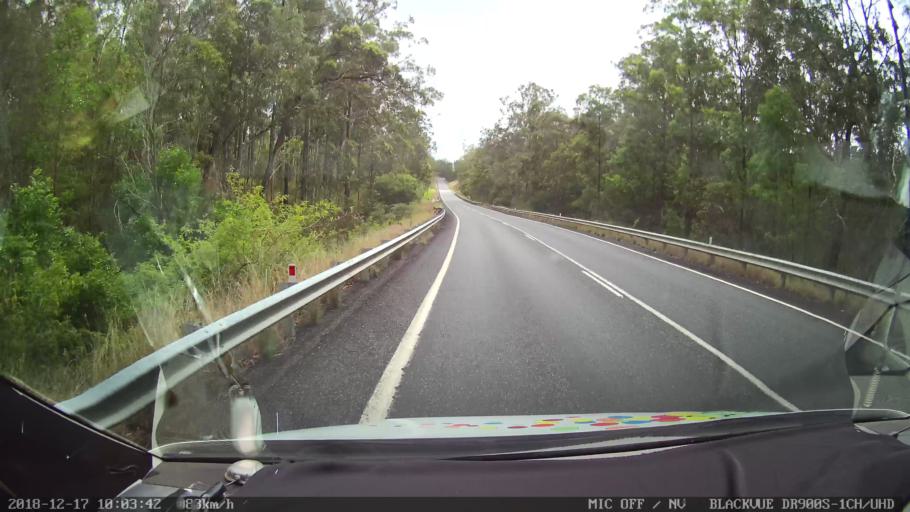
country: AU
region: New South Wales
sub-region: Tenterfield Municipality
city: Carrolls Creek
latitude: -28.8967
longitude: 152.4676
